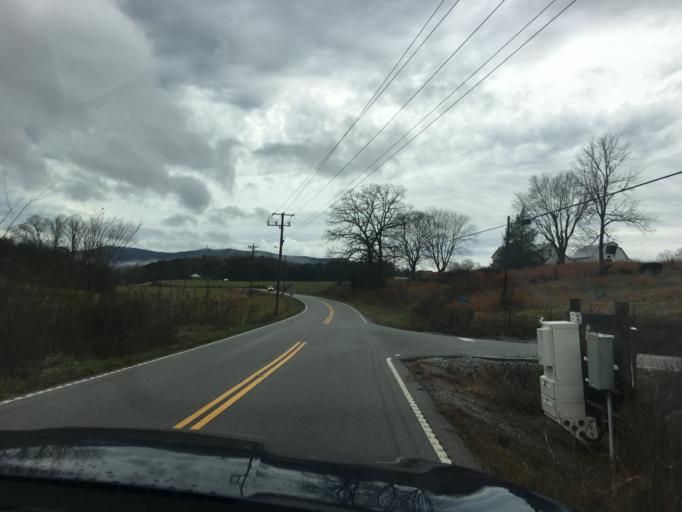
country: US
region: Tennessee
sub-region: McMinn County
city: Englewood
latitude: 35.3557
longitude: -84.3425
